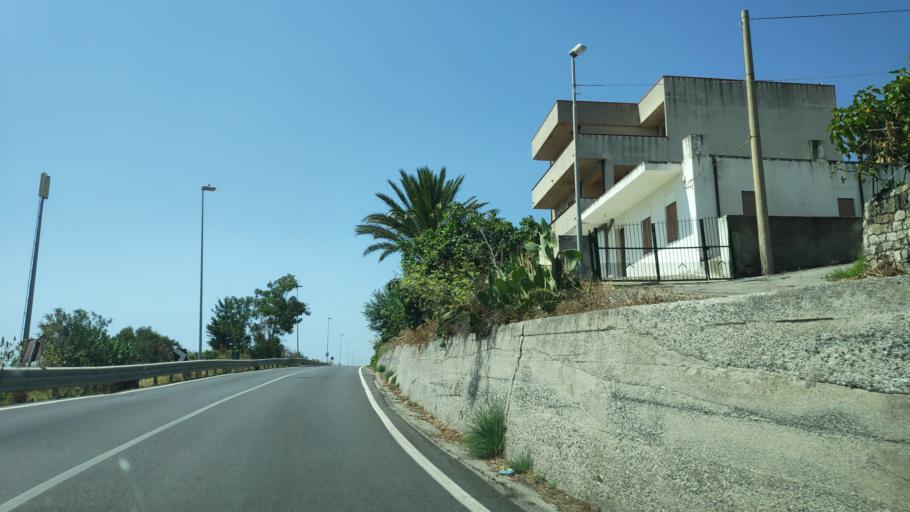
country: IT
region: Calabria
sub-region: Provincia di Reggio Calabria
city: Africo Nuovo
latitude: 38.0163
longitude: 16.1338
